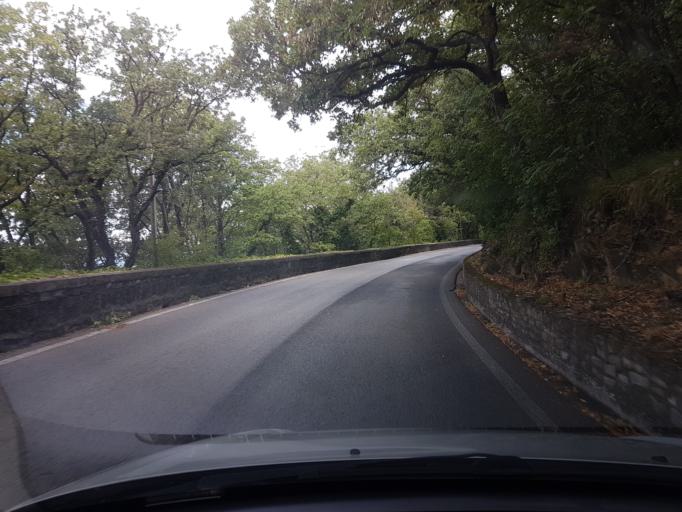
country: IT
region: Friuli Venezia Giulia
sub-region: Provincia di Trieste
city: Prosecco-Contovello
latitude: 45.6917
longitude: 13.7447
